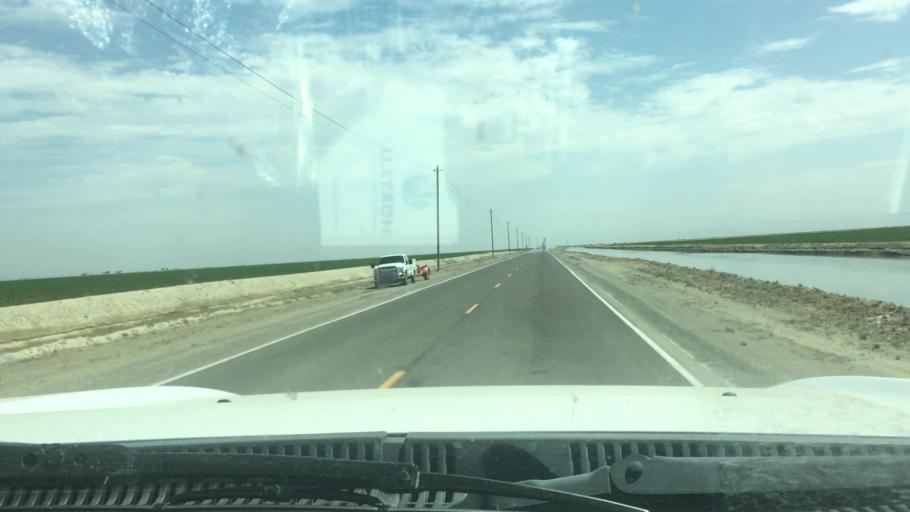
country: US
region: California
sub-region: Tulare County
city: Alpaugh
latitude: 35.8983
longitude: -119.5734
